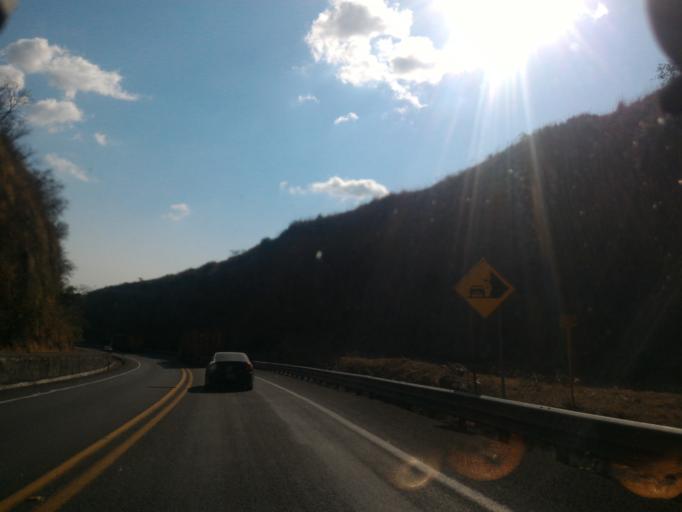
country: MX
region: Jalisco
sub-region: Tonila
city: San Marcos
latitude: 19.4503
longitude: -103.4734
